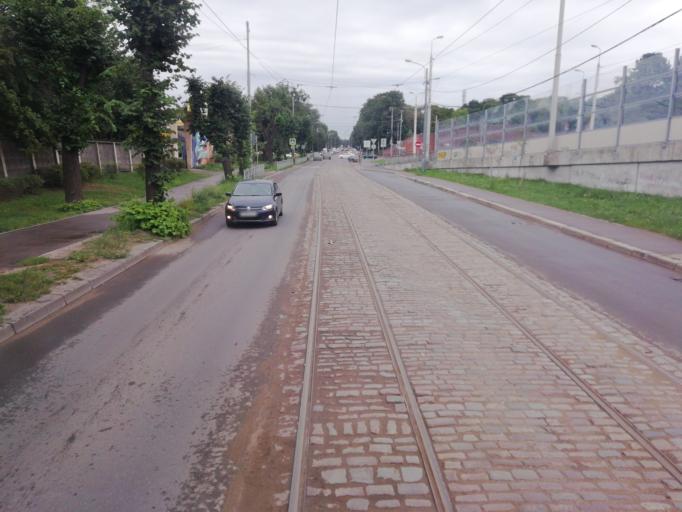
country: RU
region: Kaliningrad
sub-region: Gorod Kaliningrad
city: Kaliningrad
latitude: 54.6966
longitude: 20.5205
